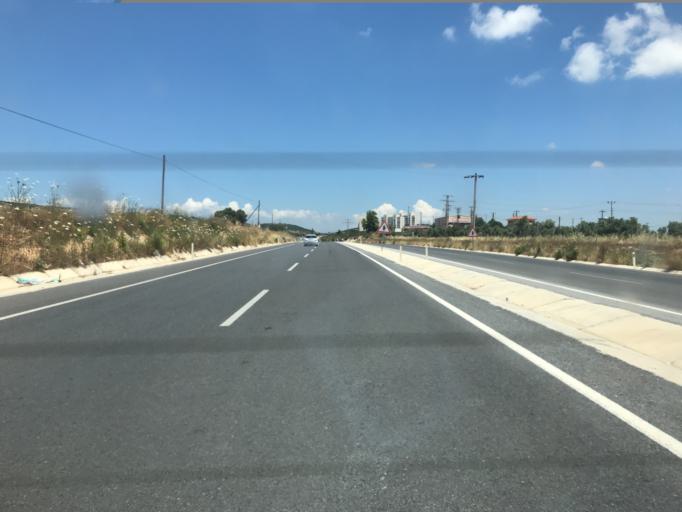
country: TR
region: Aydin
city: Akkoy
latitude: 37.4681
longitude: 27.3392
